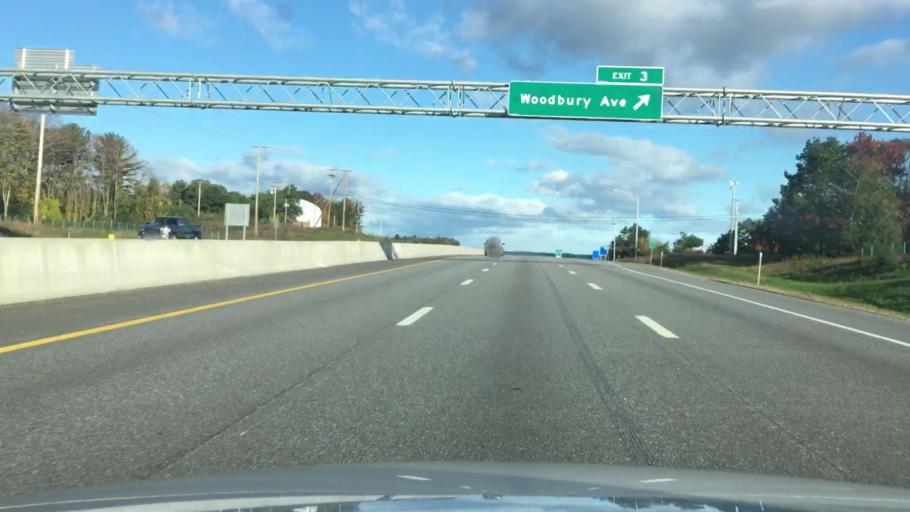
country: US
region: Maine
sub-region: York County
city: South Eliot
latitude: 43.0986
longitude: -70.8097
